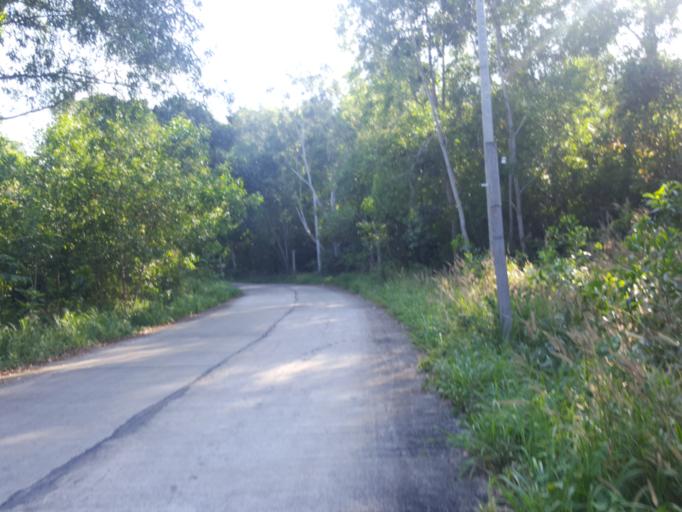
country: VN
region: Kien Giang
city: Duong GJong
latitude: 10.0586
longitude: 104.0331
